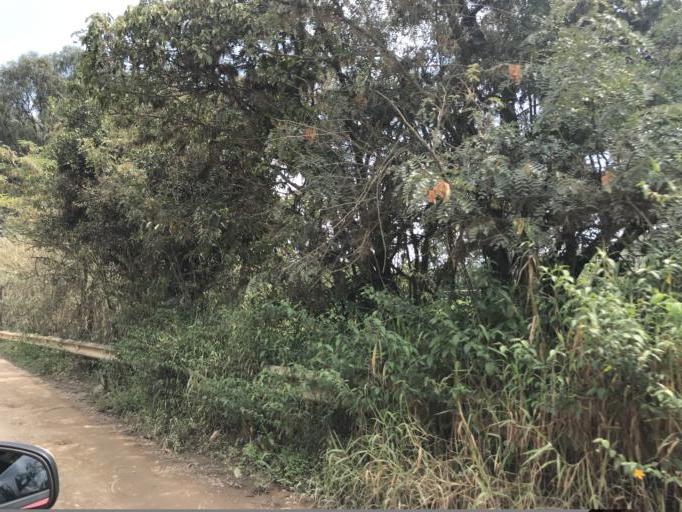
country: CO
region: Boyaca
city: Villa de Leiva
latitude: 5.6518
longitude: -73.5761
